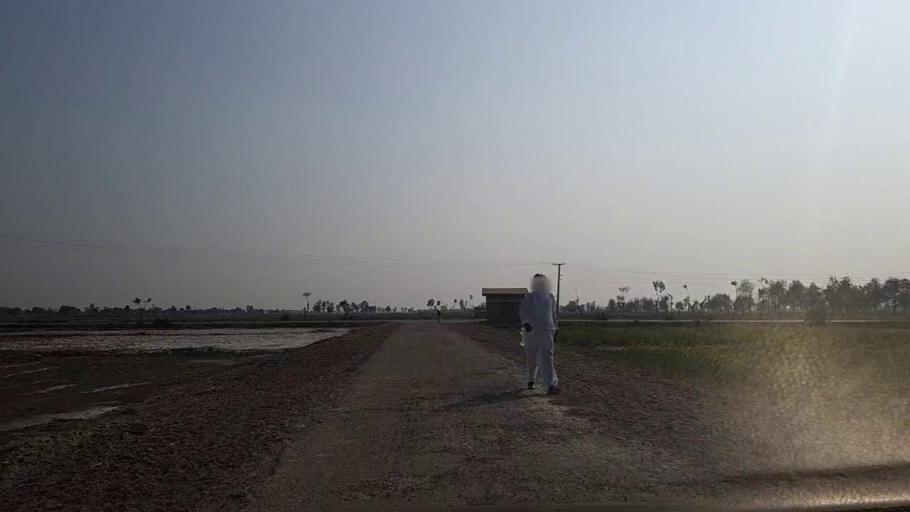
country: PK
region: Sindh
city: Daur
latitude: 26.4099
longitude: 68.4125
